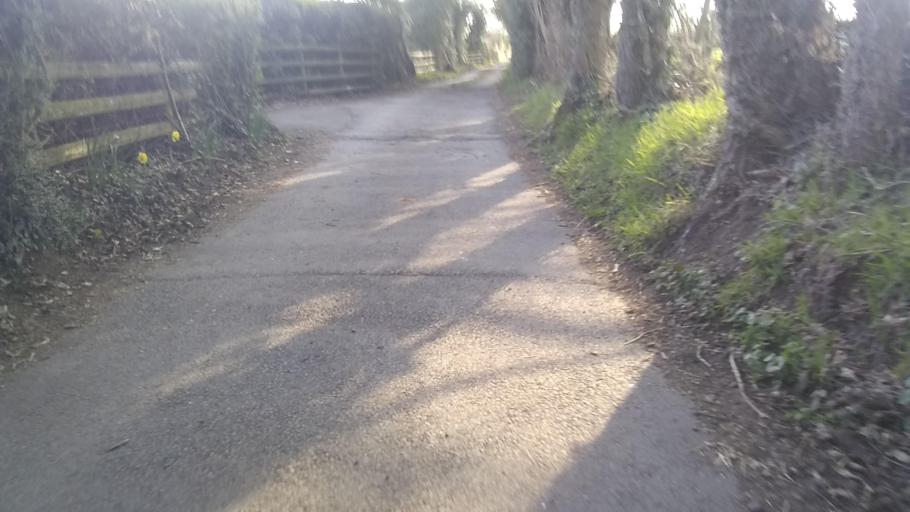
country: GB
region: England
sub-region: Worcestershire
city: Bewdley
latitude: 52.3713
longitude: -2.3918
